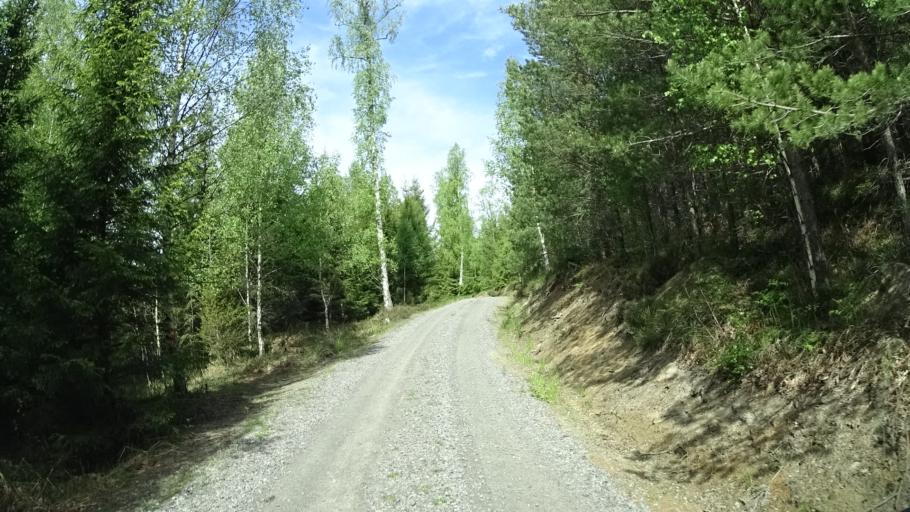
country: SE
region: OEstergoetland
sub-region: Finspangs Kommun
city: Finspang
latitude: 58.7952
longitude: 15.8542
